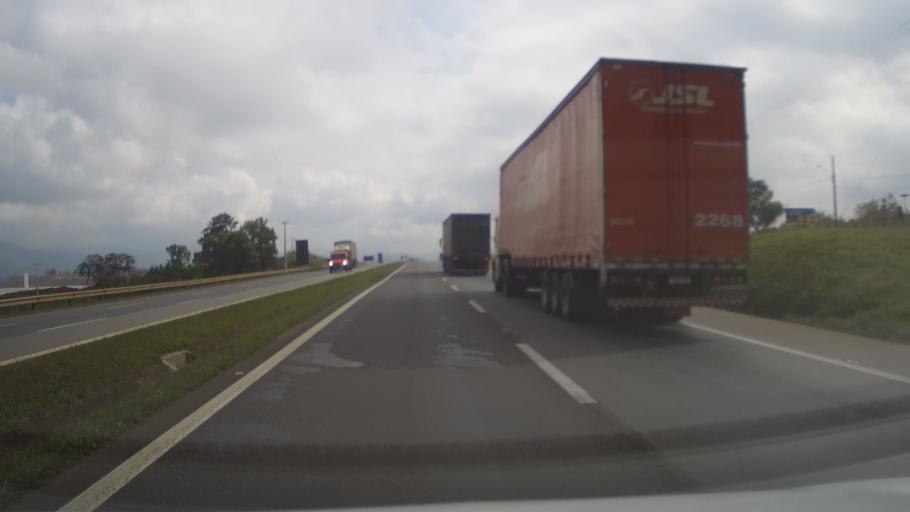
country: BR
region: Minas Gerais
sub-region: Extrema
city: Extrema
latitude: -22.8401
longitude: -46.3289
